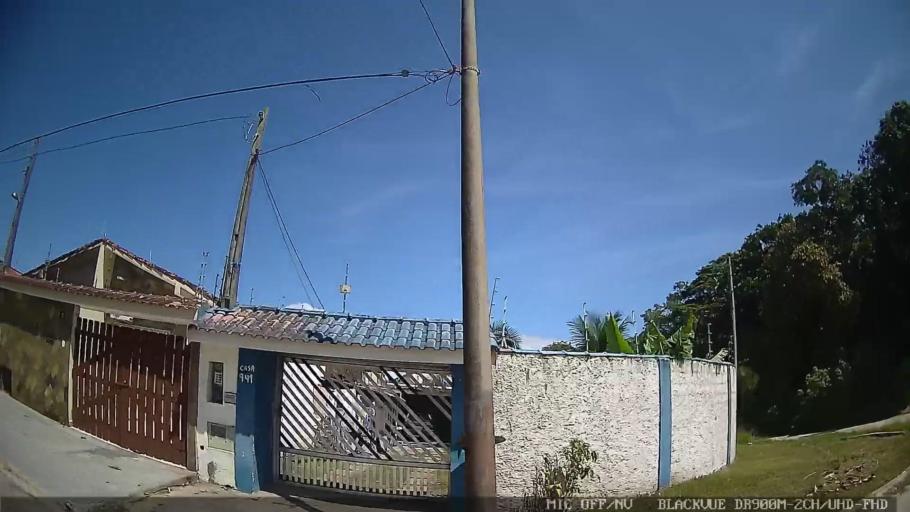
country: BR
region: Sao Paulo
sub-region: Peruibe
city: Peruibe
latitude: -24.2966
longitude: -46.9959
